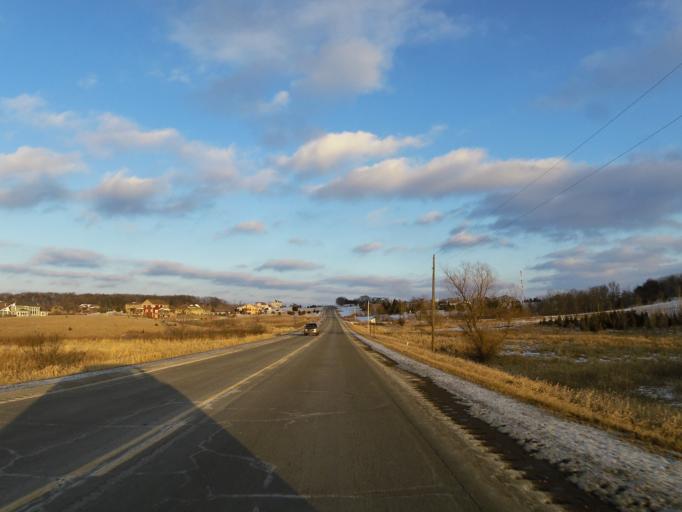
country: US
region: Minnesota
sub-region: Scott County
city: Prior Lake
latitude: 44.6342
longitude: -93.3926
